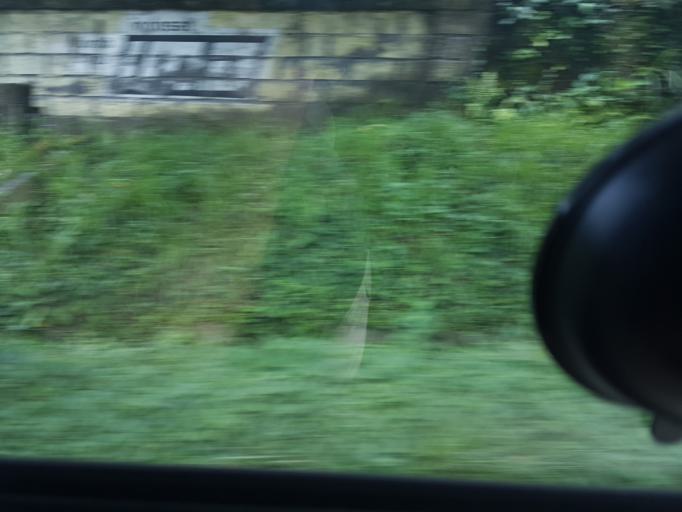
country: ID
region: Bali
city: Banjar Pesalakan
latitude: -8.5072
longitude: 115.2934
